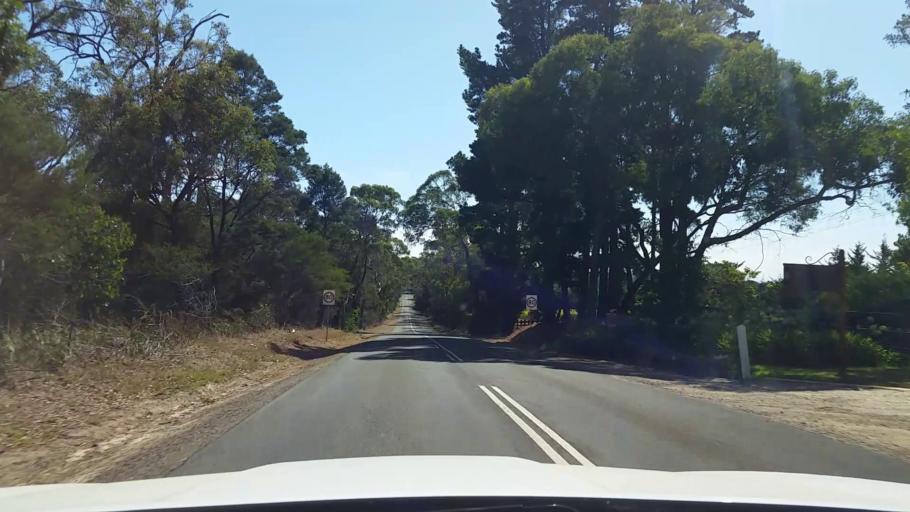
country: AU
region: Victoria
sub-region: Mornington Peninsula
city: Hastings
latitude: -38.3183
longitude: 145.1457
